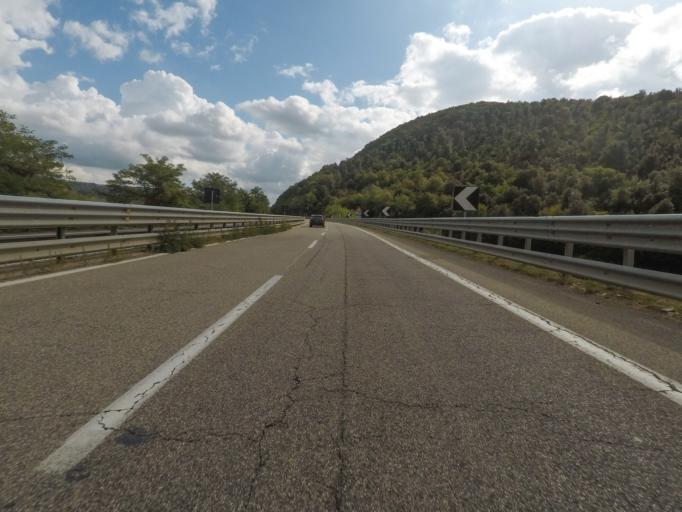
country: IT
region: Tuscany
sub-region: Provincia di Siena
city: Rapolano Terme
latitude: 43.2901
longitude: 11.6139
